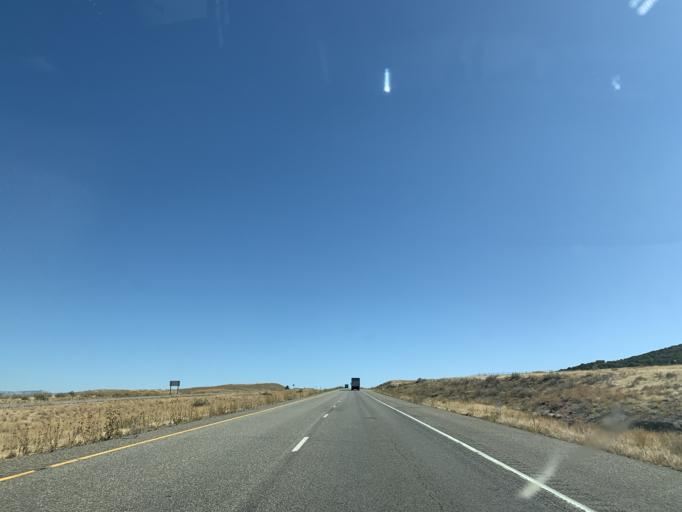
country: US
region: Colorado
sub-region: Mesa County
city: Loma
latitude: 39.2201
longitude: -108.8836
